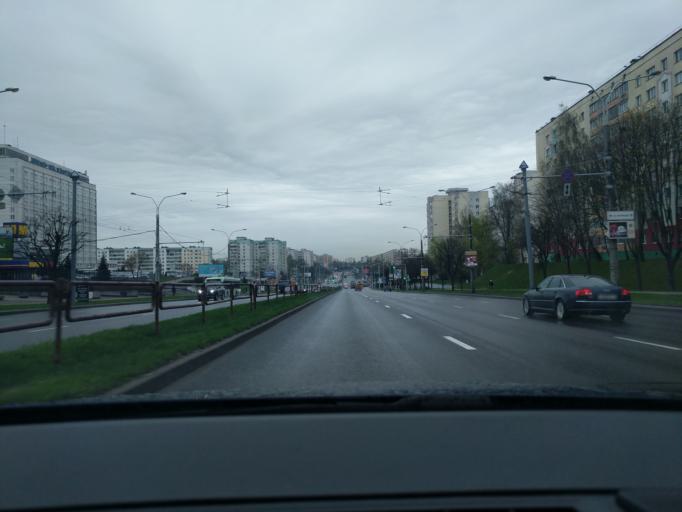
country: BY
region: Minsk
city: Novoye Medvezhino
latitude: 53.9064
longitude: 27.4961
